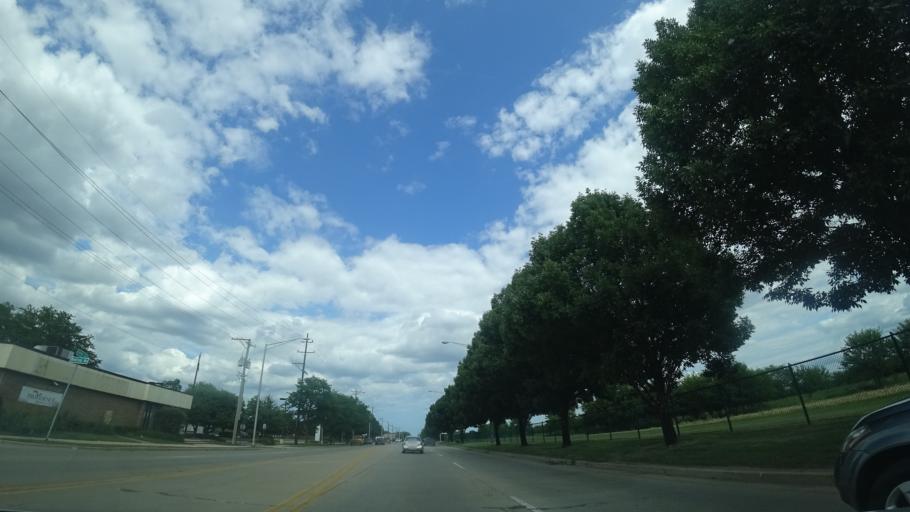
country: US
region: Illinois
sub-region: Cook County
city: Alsip
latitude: 41.6909
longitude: -87.7387
